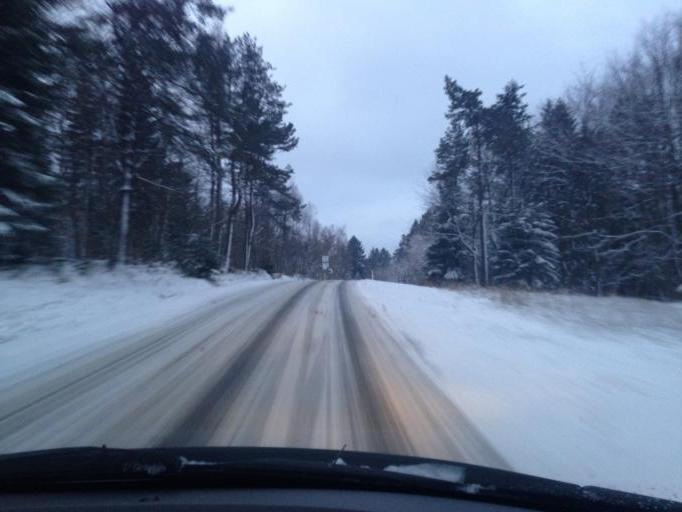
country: PL
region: Subcarpathian Voivodeship
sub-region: Powiat jasielski
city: Krempna
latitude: 49.5347
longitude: 21.4995
